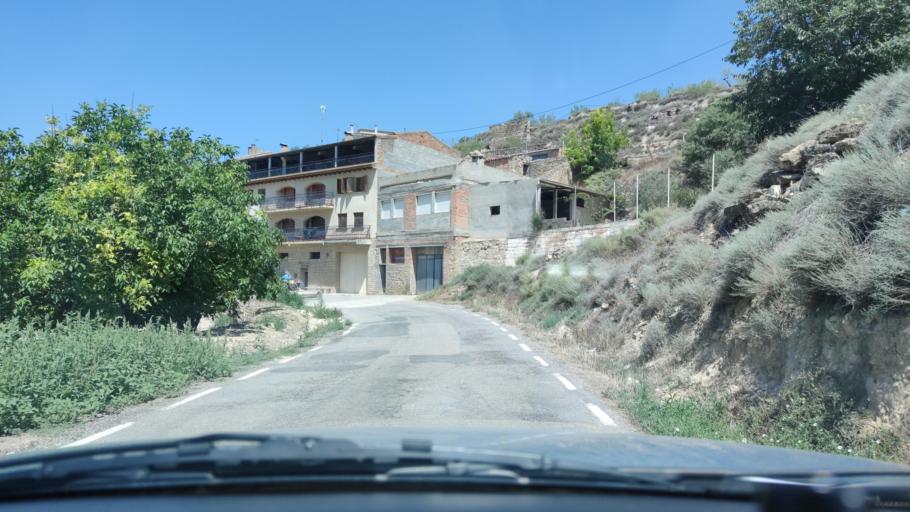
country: ES
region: Catalonia
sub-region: Provincia de Lleida
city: Fulleda
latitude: 41.4928
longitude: 1.0086
